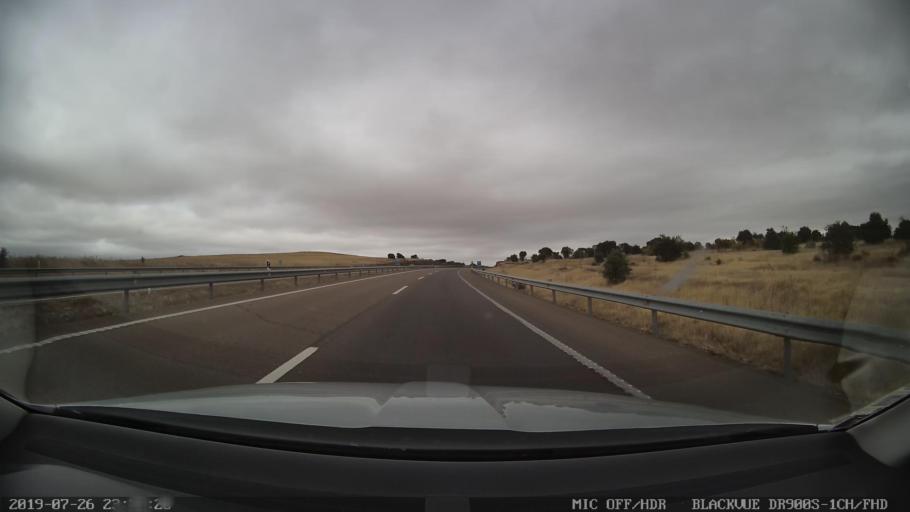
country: ES
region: Extremadura
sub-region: Provincia de Caceres
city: Santa Cruz de la Sierra
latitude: 39.3742
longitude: -5.8796
